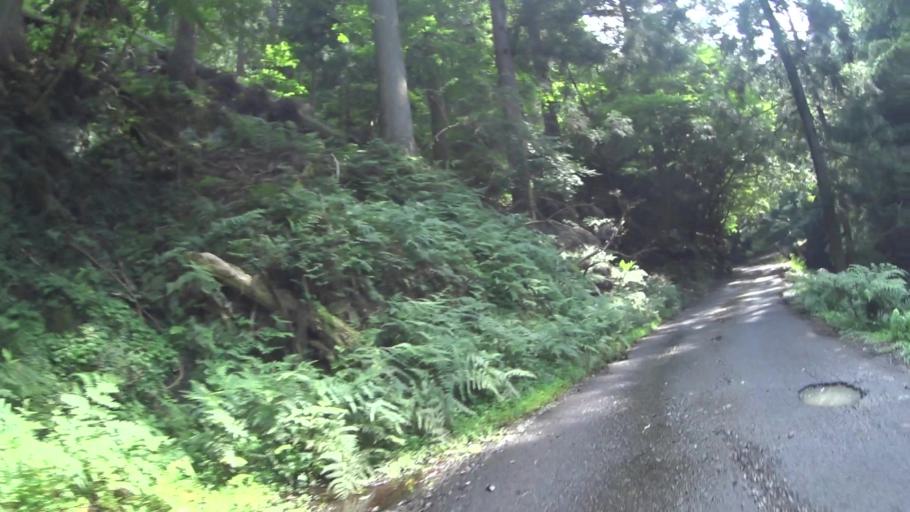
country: JP
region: Fukui
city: Obama
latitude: 35.2886
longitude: 135.6459
